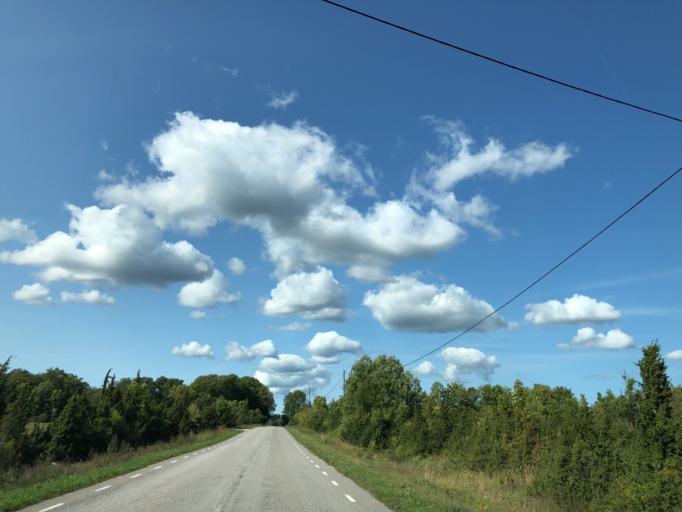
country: EE
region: Hiiumaa
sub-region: Kaerdla linn
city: Kardla
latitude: 58.7944
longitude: 22.7677
